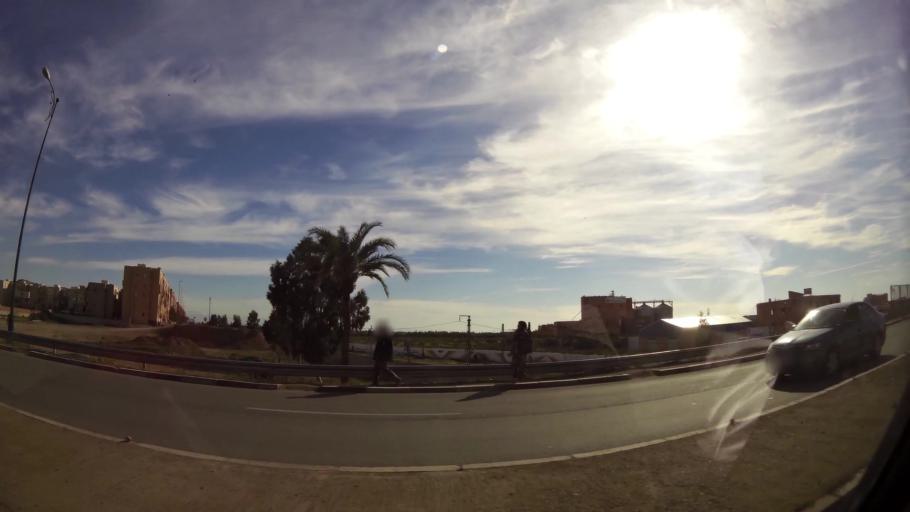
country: MA
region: Marrakech-Tensift-Al Haouz
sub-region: Marrakech
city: Marrakesh
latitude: 31.6653
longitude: -8.0337
